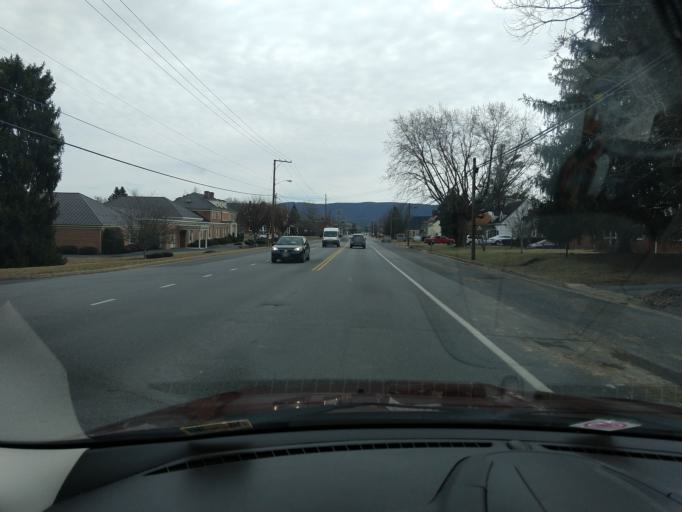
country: US
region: Virginia
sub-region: City of Waynesboro
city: Waynesboro
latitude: 38.0741
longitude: -78.9062
